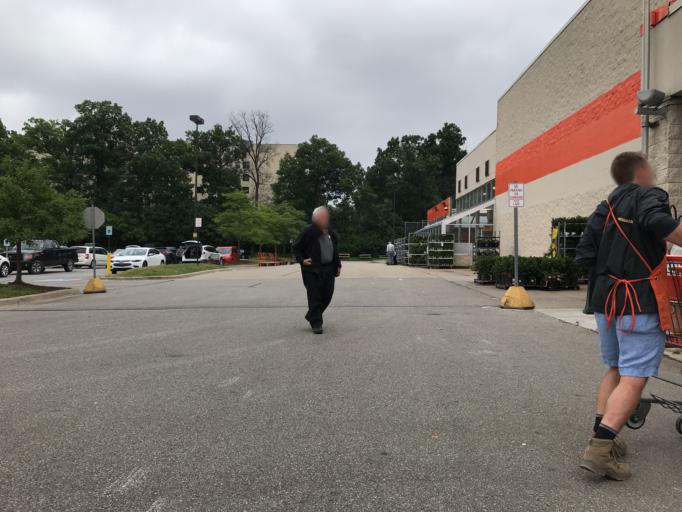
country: US
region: Michigan
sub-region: Washtenaw County
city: Ypsilanti
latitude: 42.2406
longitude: -83.6821
